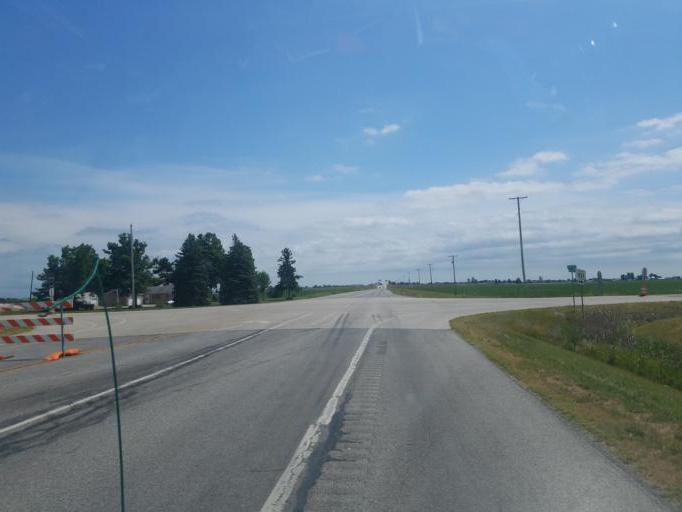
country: US
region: Indiana
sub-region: Allen County
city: Woodburn
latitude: 41.1547
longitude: -84.8488
